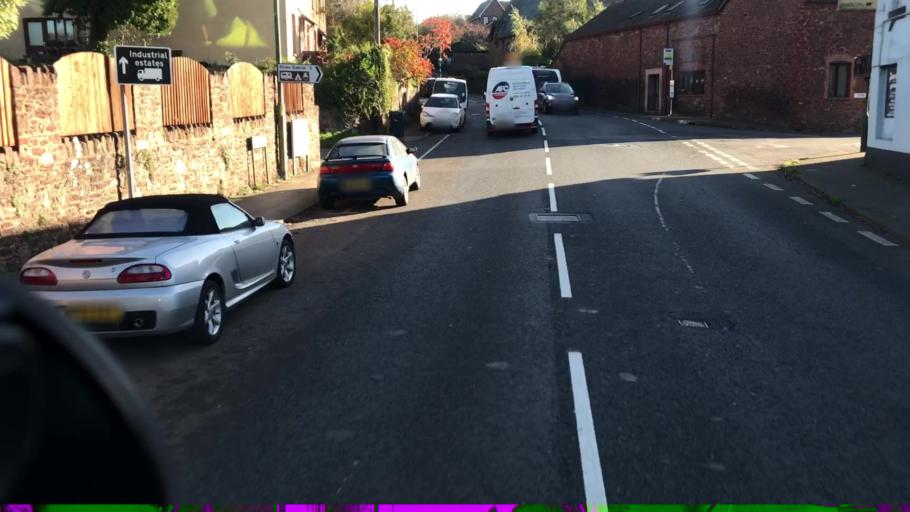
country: GB
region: England
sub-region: Devon
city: Marldon
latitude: 50.4288
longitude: -3.5973
